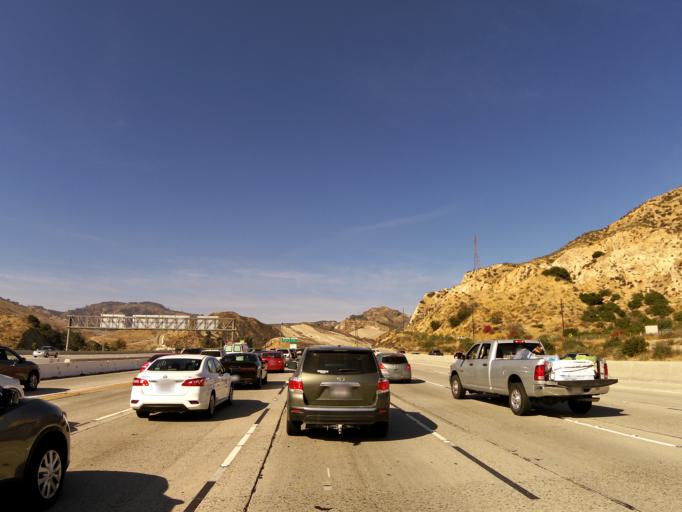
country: US
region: California
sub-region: Los Angeles County
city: San Fernando
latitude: 34.3225
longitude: -118.4986
